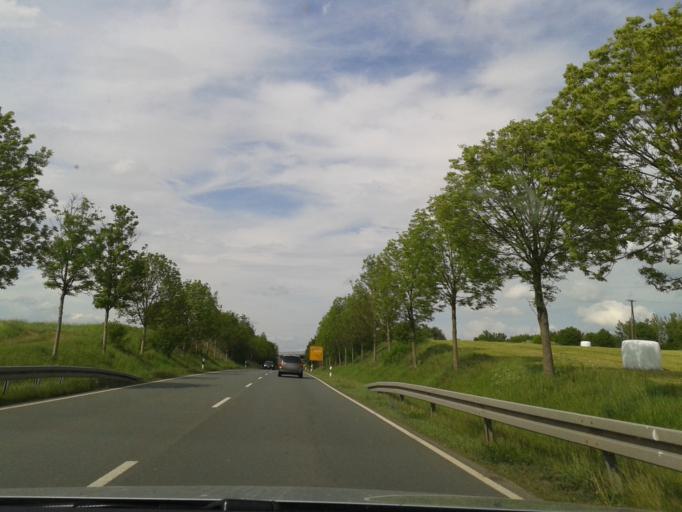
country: DE
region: Hesse
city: Frankenberg
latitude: 51.0480
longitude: 8.8136
